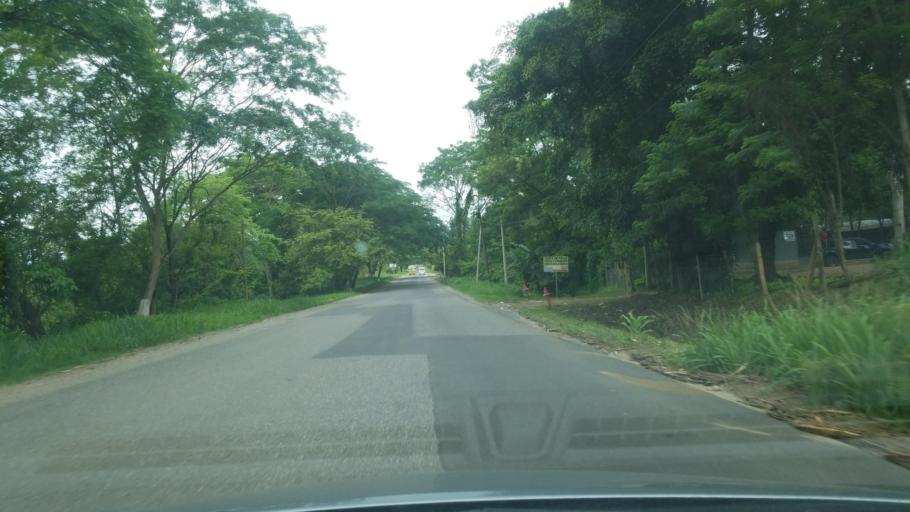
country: HN
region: Santa Barbara
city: La Flecha
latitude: 15.2960
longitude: -88.4602
